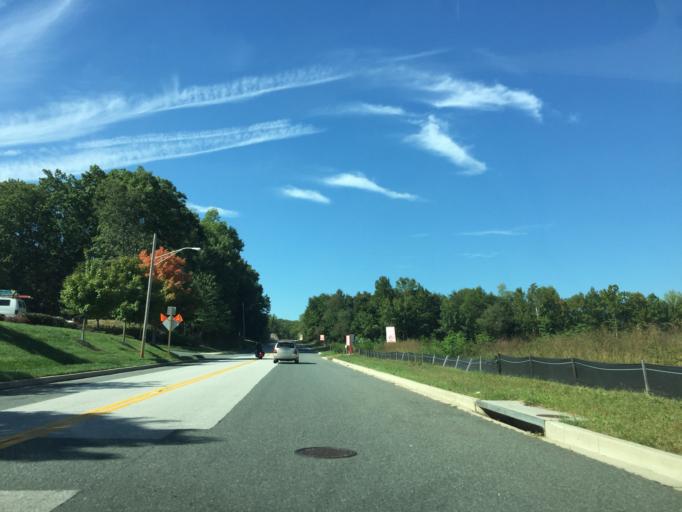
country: US
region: Maryland
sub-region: Baltimore County
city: White Marsh
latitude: 39.4076
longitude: -76.4132
